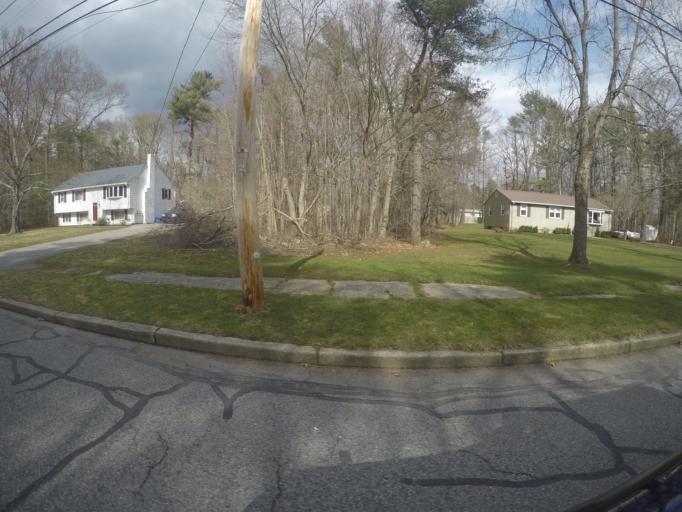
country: US
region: Massachusetts
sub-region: Bristol County
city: Easton
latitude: 42.0371
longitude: -71.1145
